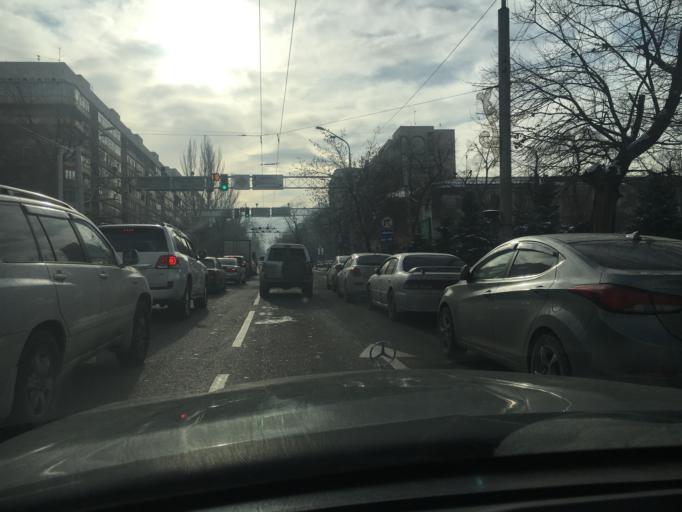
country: KZ
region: Almaty Qalasy
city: Almaty
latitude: 43.2494
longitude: 76.9334
